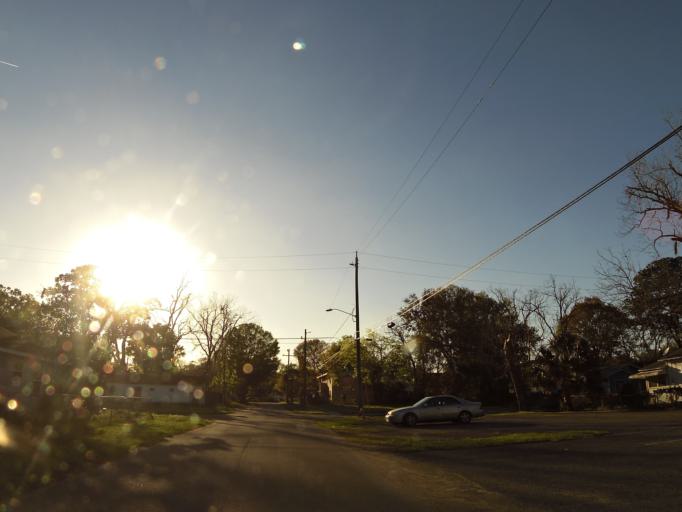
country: US
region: Florida
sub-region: Duval County
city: Jacksonville
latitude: 30.3396
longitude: -81.6848
